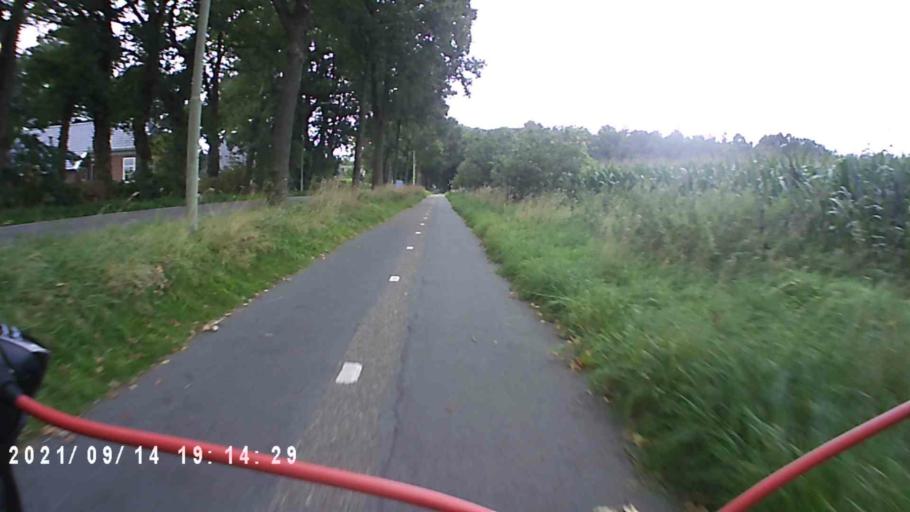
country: NL
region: Drenthe
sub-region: Gemeente Aa en Hunze
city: Anloo
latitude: 53.0688
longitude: 6.7057
